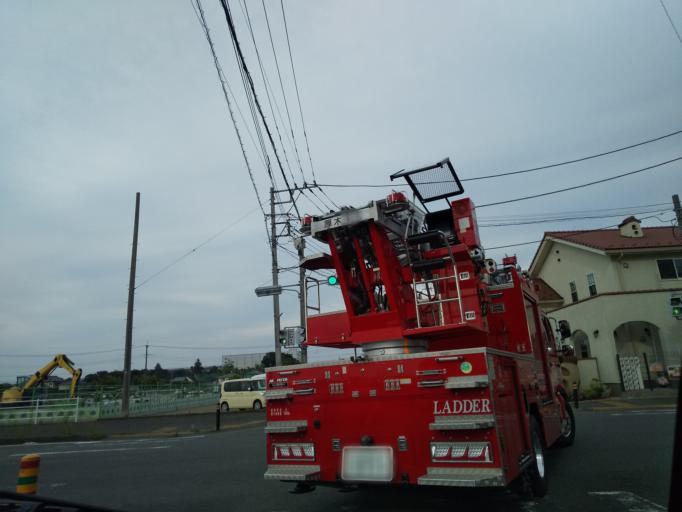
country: JP
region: Kanagawa
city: Atsugi
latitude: 35.4695
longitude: 139.3588
